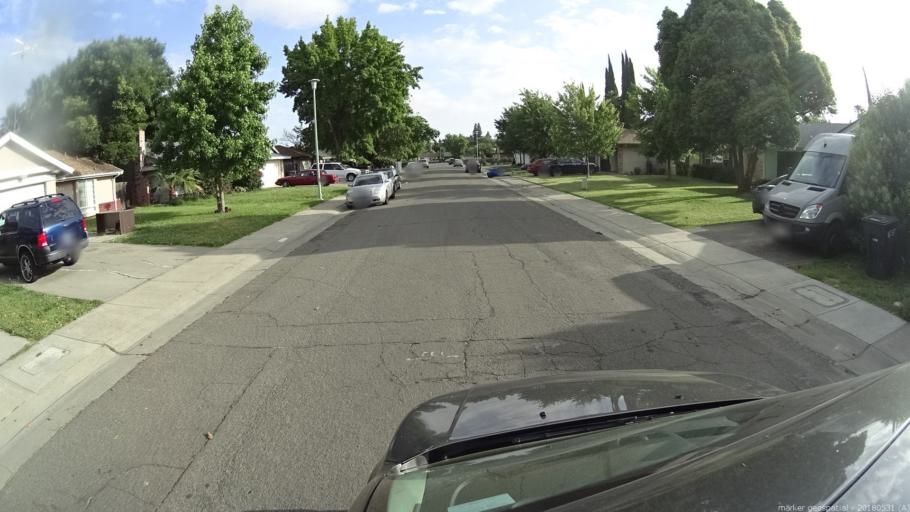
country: US
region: California
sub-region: Sacramento County
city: Sacramento
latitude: 38.6253
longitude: -121.4881
